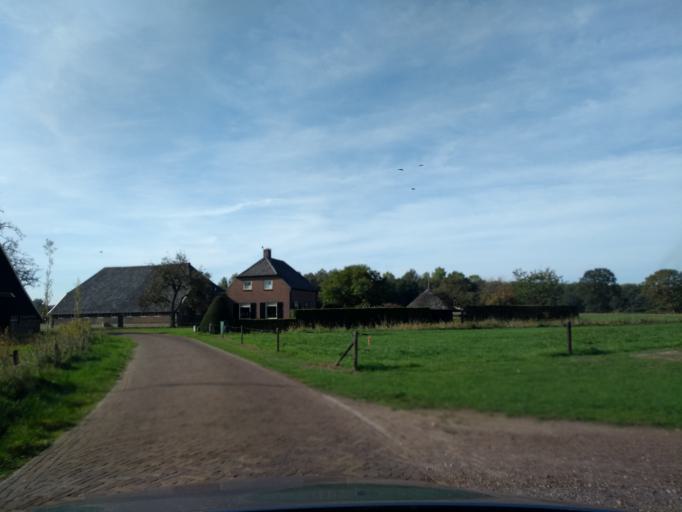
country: NL
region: Gelderland
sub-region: Gemeente Lochem
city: Barchem
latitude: 52.0884
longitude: 6.3949
